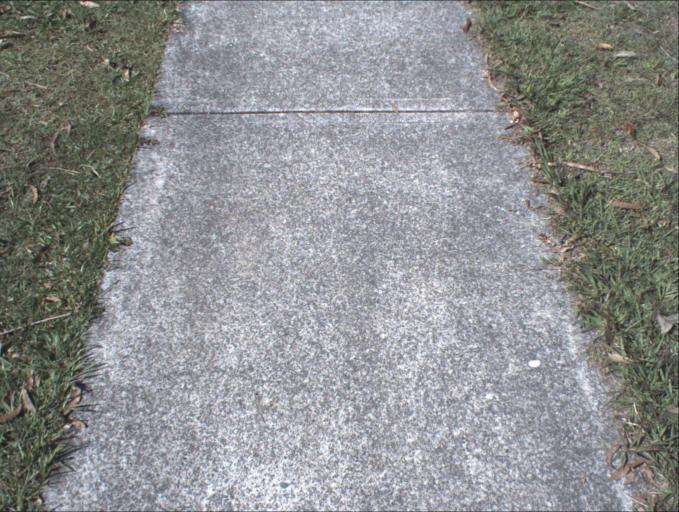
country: AU
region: Queensland
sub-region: Logan
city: Slacks Creek
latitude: -27.6454
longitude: 153.1338
